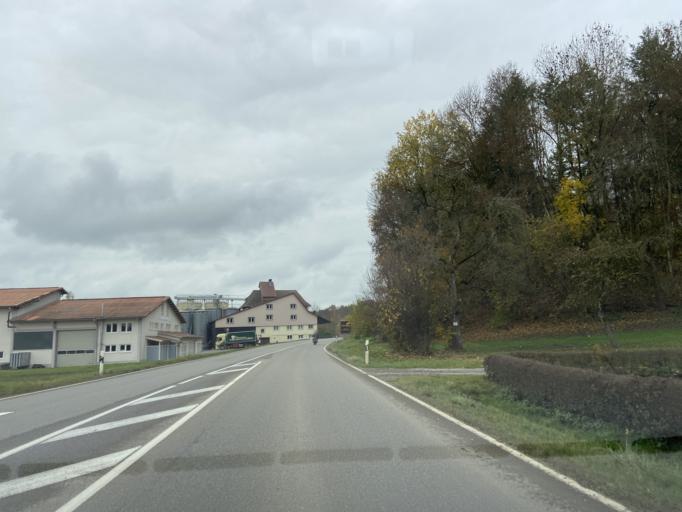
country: DE
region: Baden-Wuerttemberg
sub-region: Tuebingen Region
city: Krauchenwies
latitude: 47.9989
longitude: 9.2366
